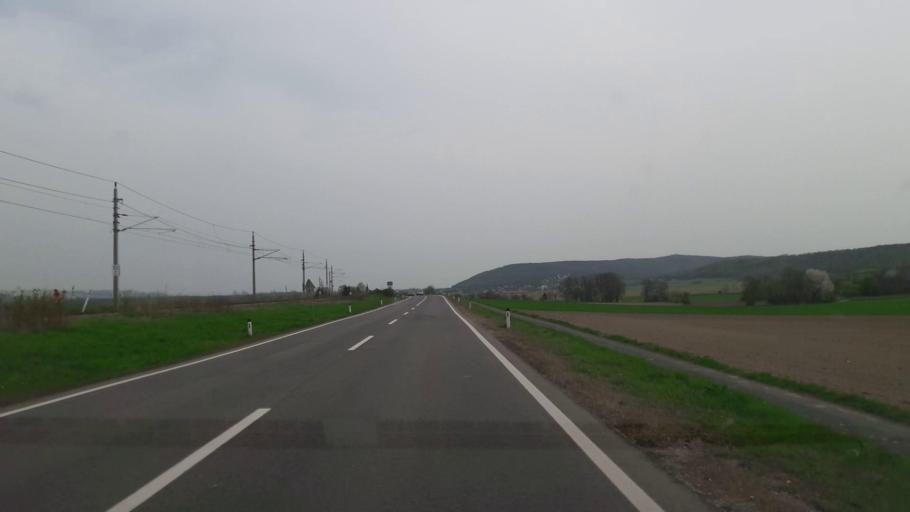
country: AT
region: Lower Austria
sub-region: Politischer Bezirk Bruck an der Leitha
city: Hainburg an der Donau
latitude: 48.1450
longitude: 16.9682
